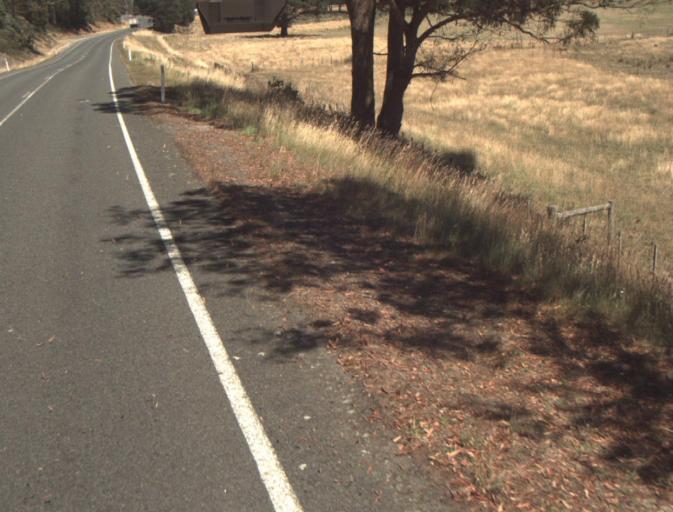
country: AU
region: Tasmania
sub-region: Dorset
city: Scottsdale
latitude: -41.3168
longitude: 147.3663
